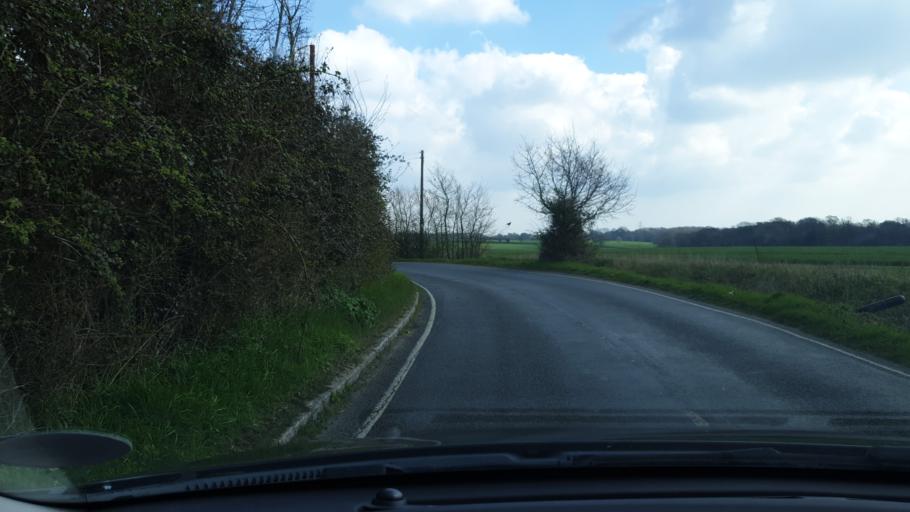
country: GB
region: England
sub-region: Essex
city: Great Bentley
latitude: 51.8686
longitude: 1.1028
